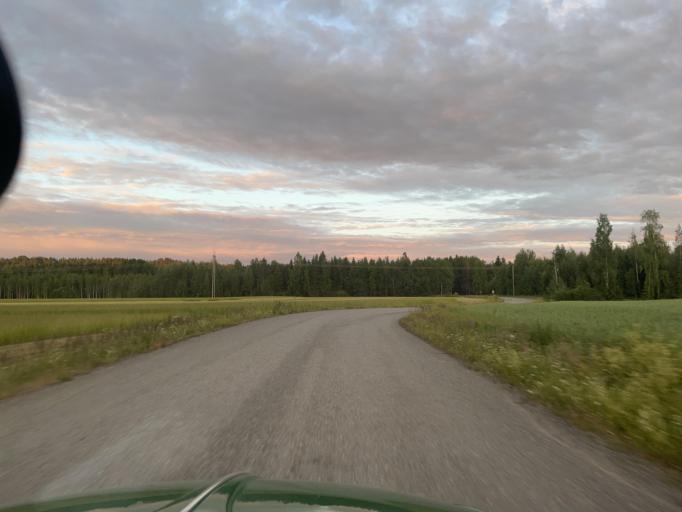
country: FI
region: Uusimaa
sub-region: Helsinki
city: Lohja
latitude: 60.2296
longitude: 24.0747
